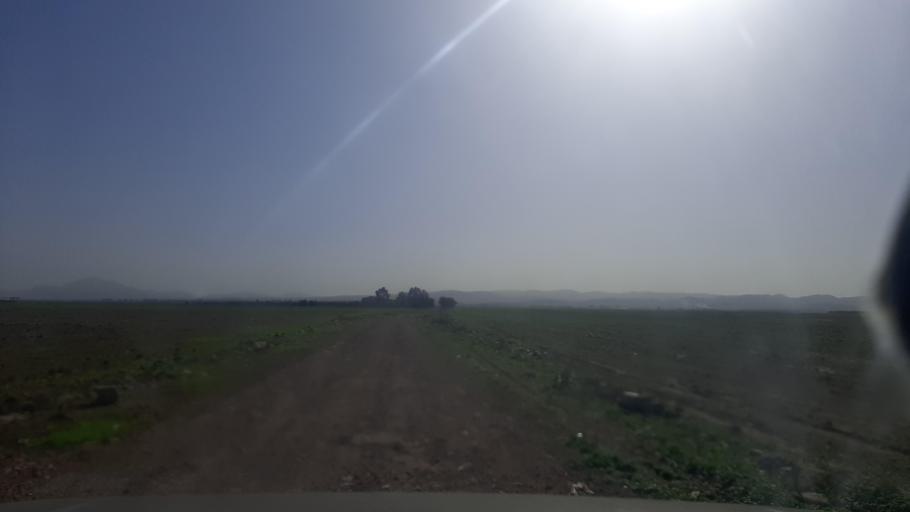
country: TN
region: Tunis
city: La Mohammedia
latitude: 36.6463
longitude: 10.0884
